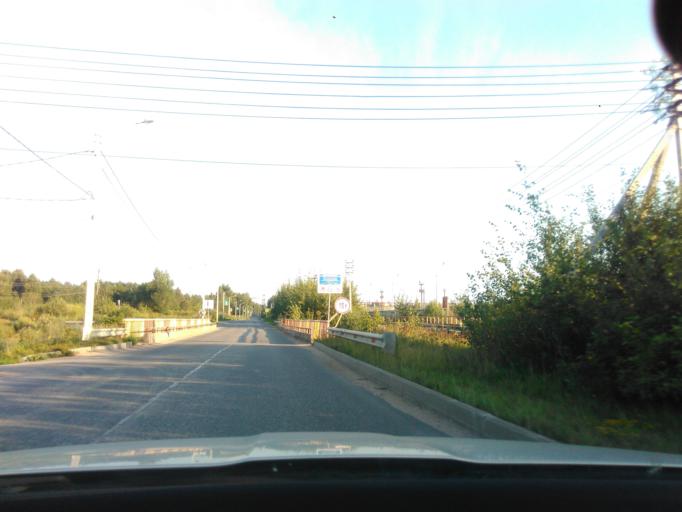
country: RU
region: Tverskaya
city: Konakovo
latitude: 56.7385
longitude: 36.7804
